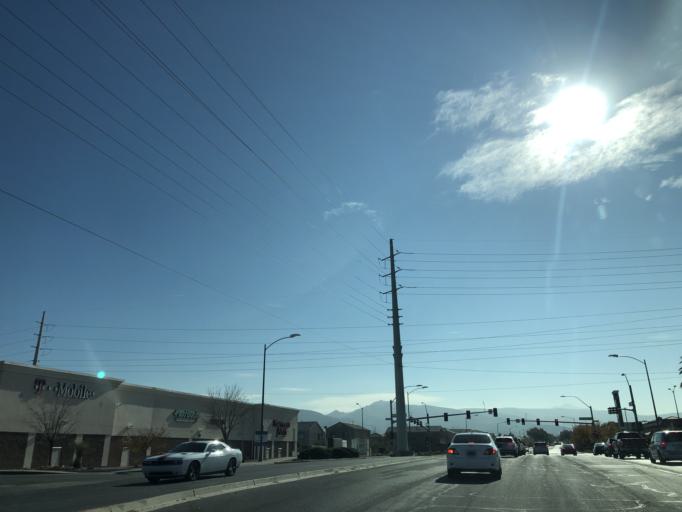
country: US
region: Nevada
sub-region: Clark County
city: Whitney
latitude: 36.0575
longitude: -115.0376
